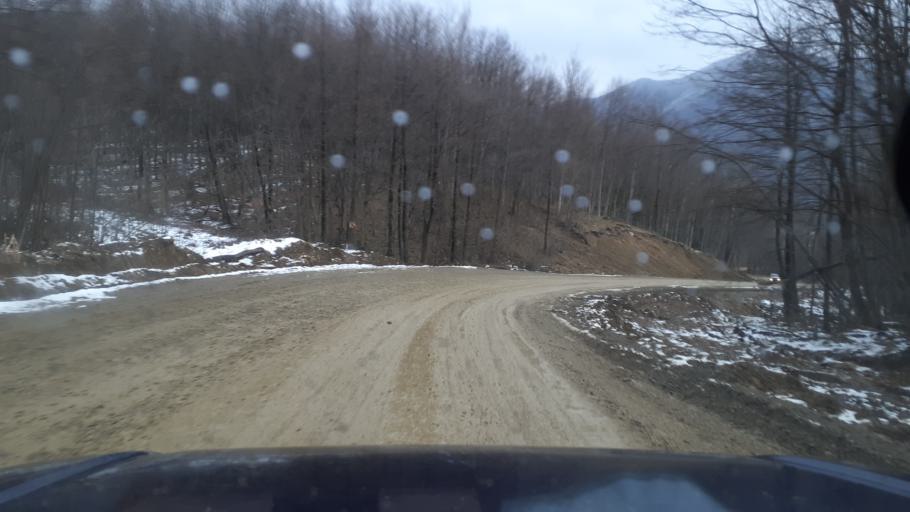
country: RU
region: Krasnodarskiy
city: Neftegorsk
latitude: 44.1653
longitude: 39.8066
